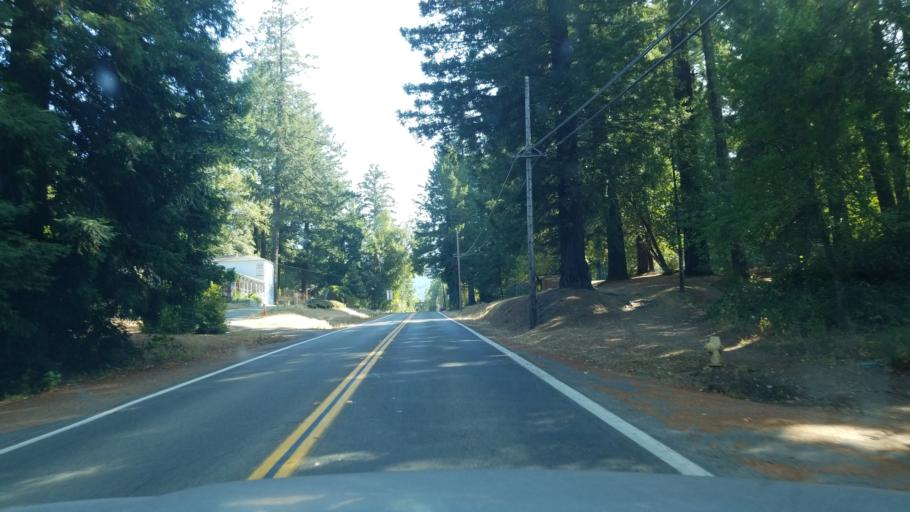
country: US
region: California
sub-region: Humboldt County
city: Redway
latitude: 40.2343
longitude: -123.8244
